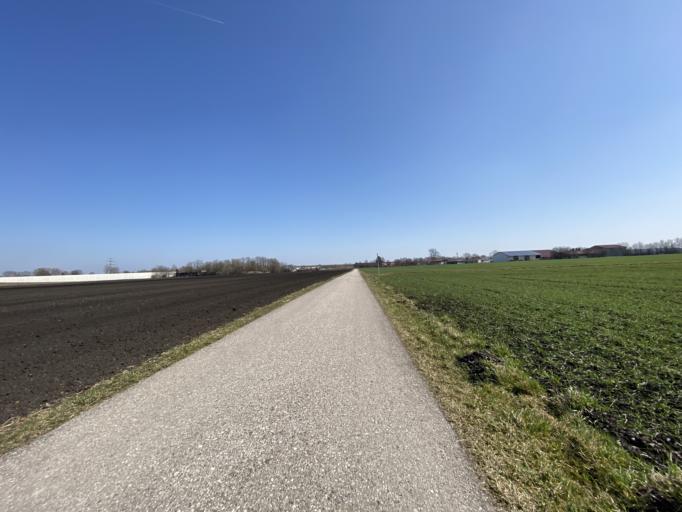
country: DE
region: Bavaria
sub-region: Upper Bavaria
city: Aschheim
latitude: 48.1884
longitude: 11.6967
